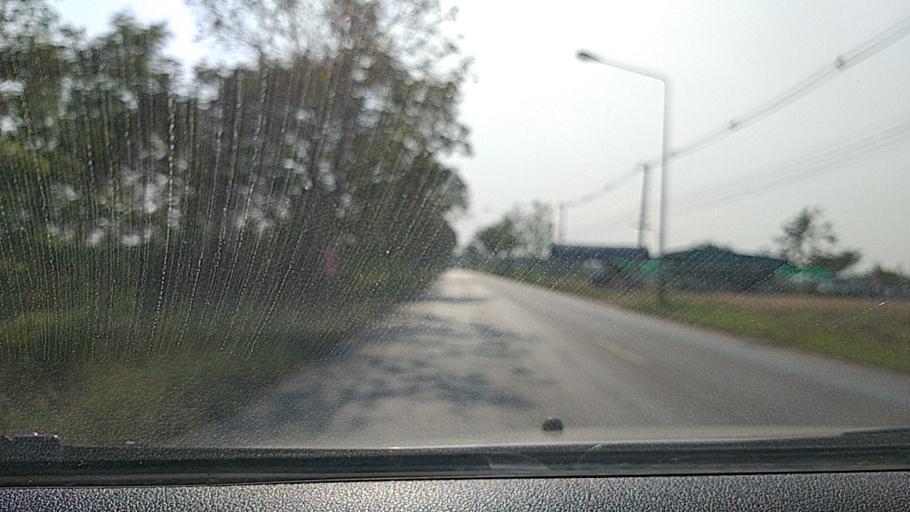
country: TH
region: Ang Thong
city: Chaiyo
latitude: 14.7226
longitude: 100.4512
